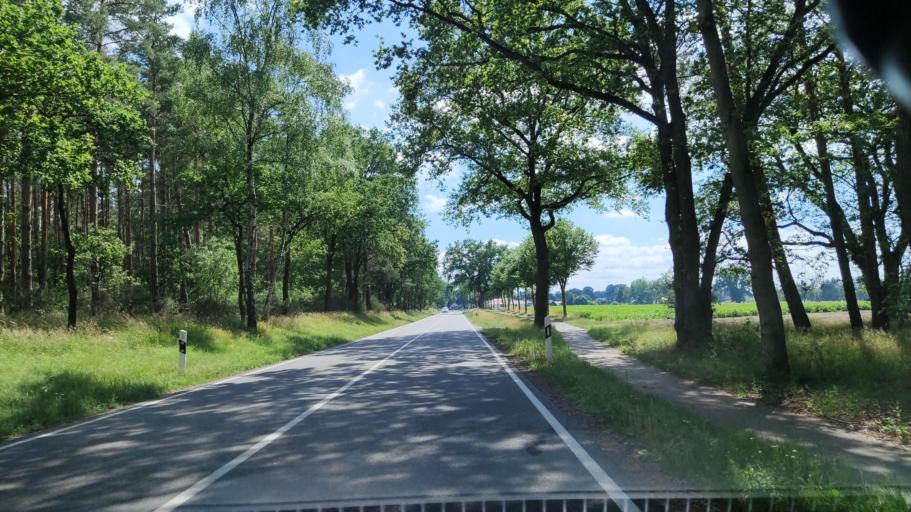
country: DE
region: Mecklenburg-Vorpommern
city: Lubtheen
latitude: 53.3117
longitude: 11.0898
